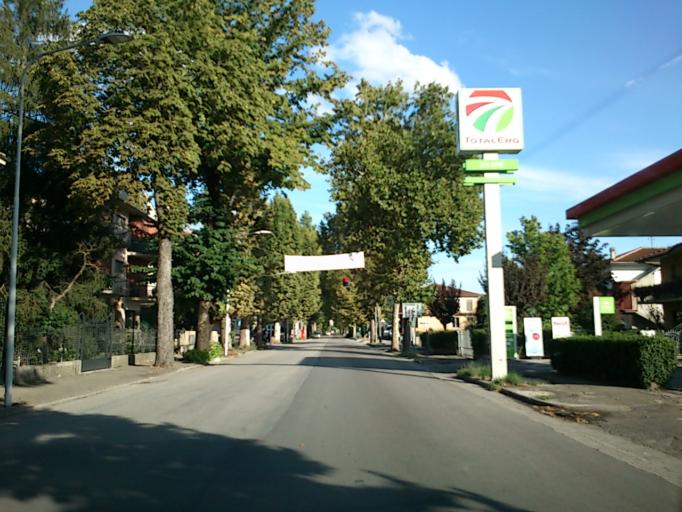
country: IT
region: The Marches
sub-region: Provincia di Pesaro e Urbino
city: Urbania
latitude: 43.6651
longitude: 12.5265
